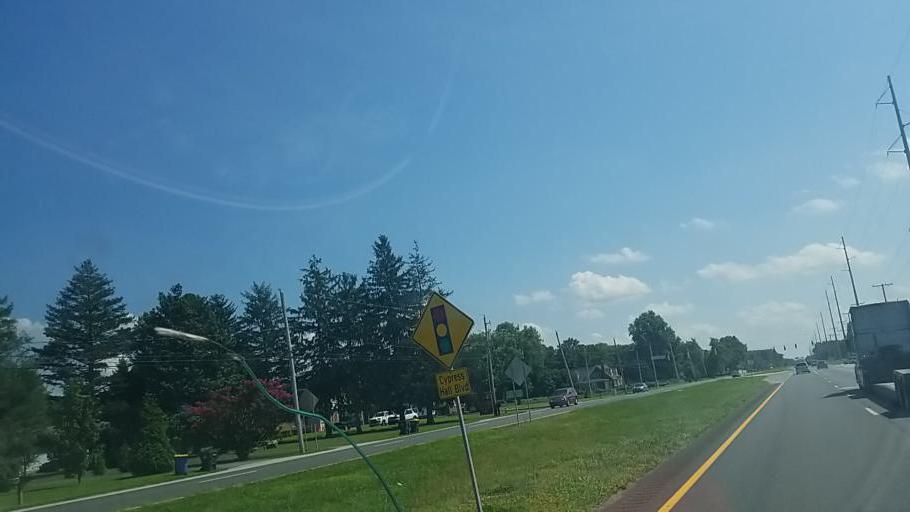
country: US
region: Delaware
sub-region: Sussex County
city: Milford
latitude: 38.8988
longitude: -75.4398
